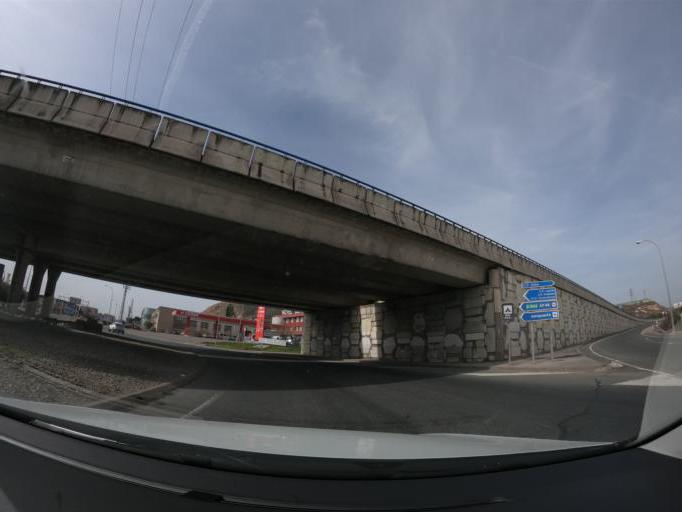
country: ES
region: La Rioja
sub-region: Provincia de La Rioja
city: Logrono
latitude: 42.4723
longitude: -2.4160
